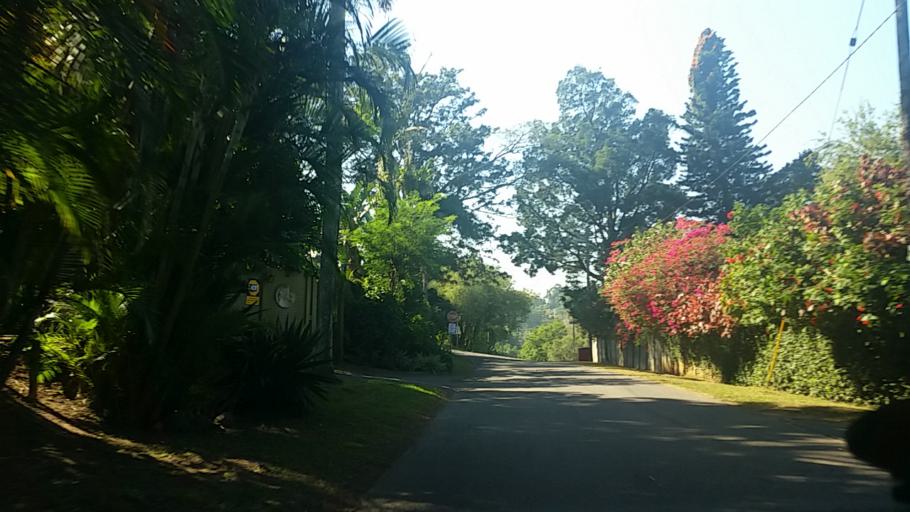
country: ZA
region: KwaZulu-Natal
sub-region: eThekwini Metropolitan Municipality
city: Berea
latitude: -29.8505
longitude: 30.9036
